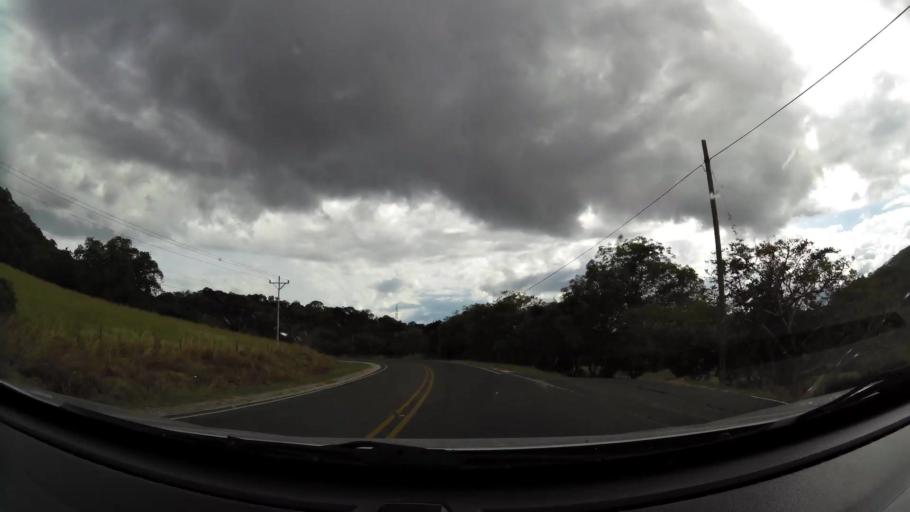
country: CR
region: Guanacaste
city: Nandayure
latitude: 10.2237
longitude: -85.2176
